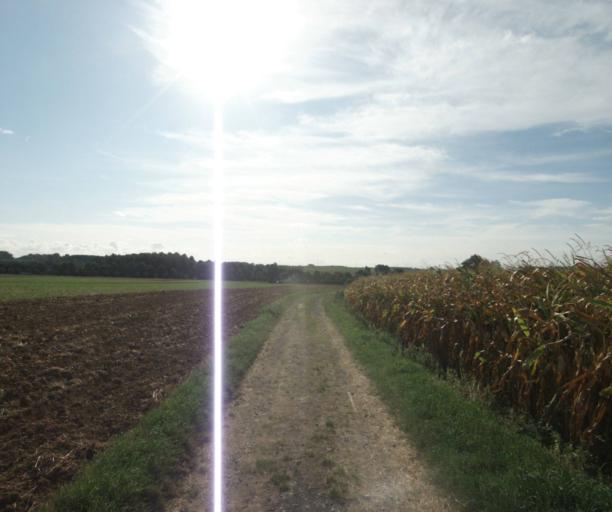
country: FR
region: Nord-Pas-de-Calais
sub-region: Departement du Nord
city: Anstaing
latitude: 50.5924
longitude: 3.1831
